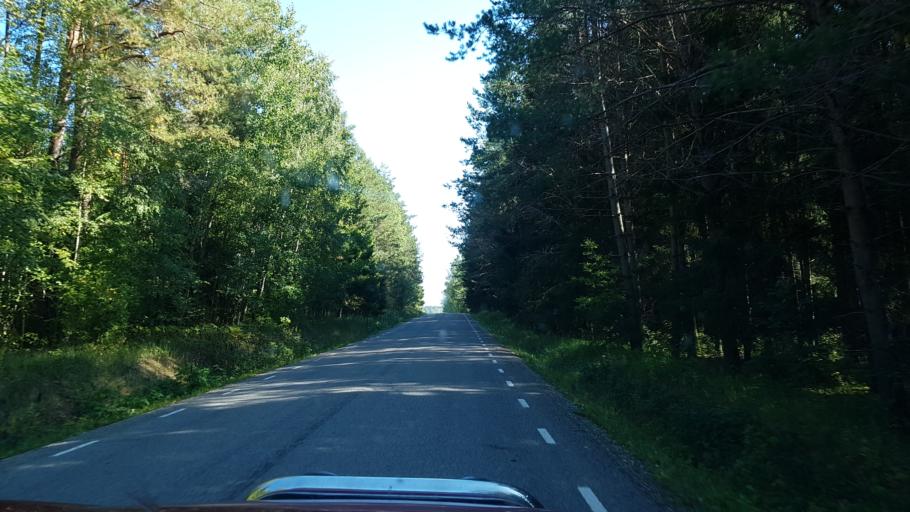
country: EE
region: Polvamaa
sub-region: Polva linn
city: Polva
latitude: 58.2101
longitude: 27.1367
